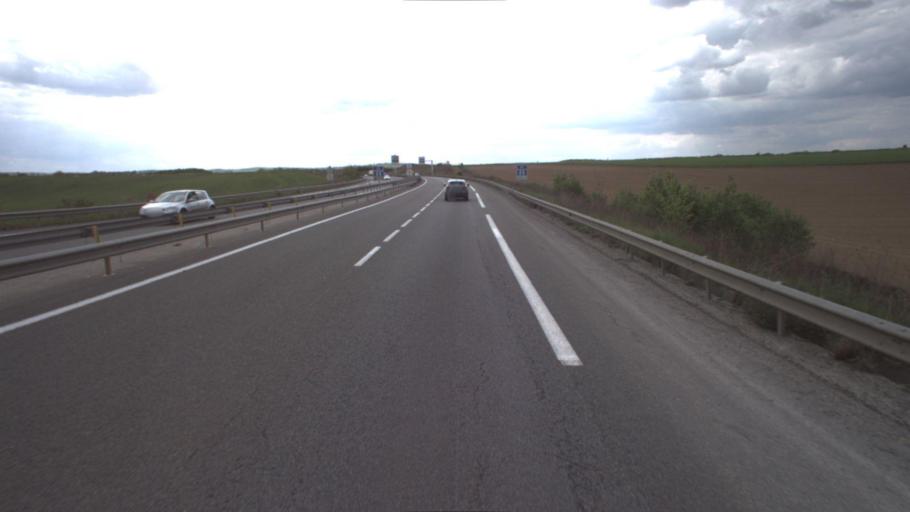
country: FR
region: Ile-de-France
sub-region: Departement de Seine-et-Marne
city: Villenoy
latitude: 48.9443
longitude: 2.8521
